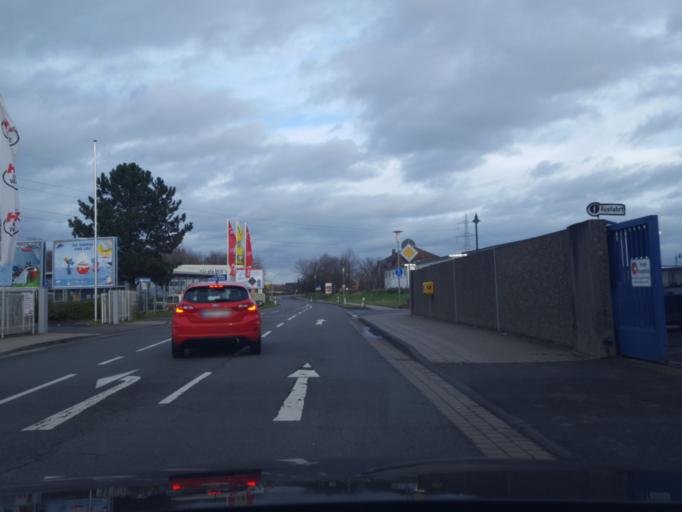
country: DE
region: North Rhine-Westphalia
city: Niederkassel
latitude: 50.7977
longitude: 7.0526
